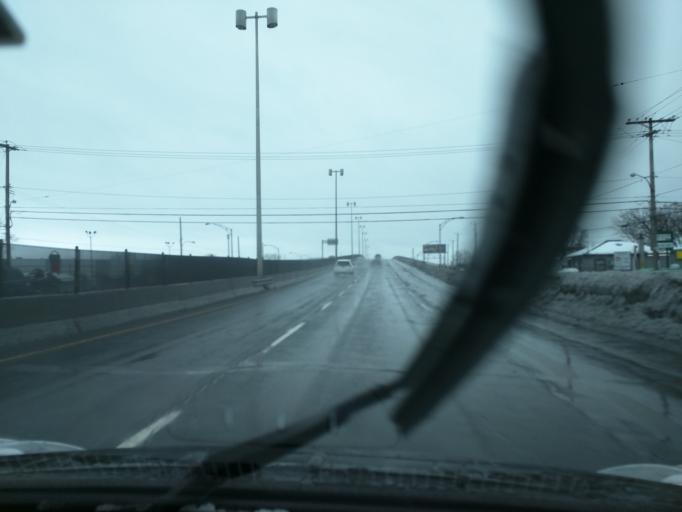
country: CA
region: Quebec
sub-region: Monteregie
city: Longueuil
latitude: 45.5151
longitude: -73.5082
